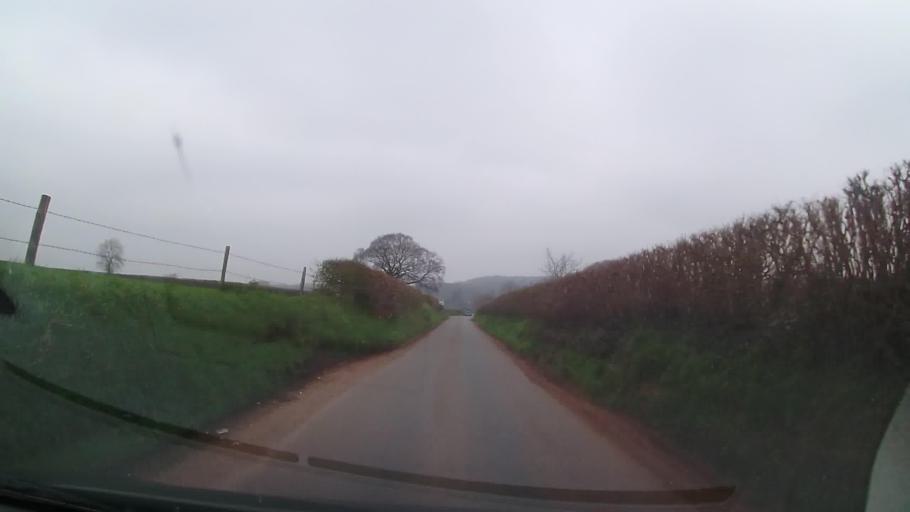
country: GB
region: England
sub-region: Staffordshire
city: Standon
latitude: 52.9407
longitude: -2.3525
